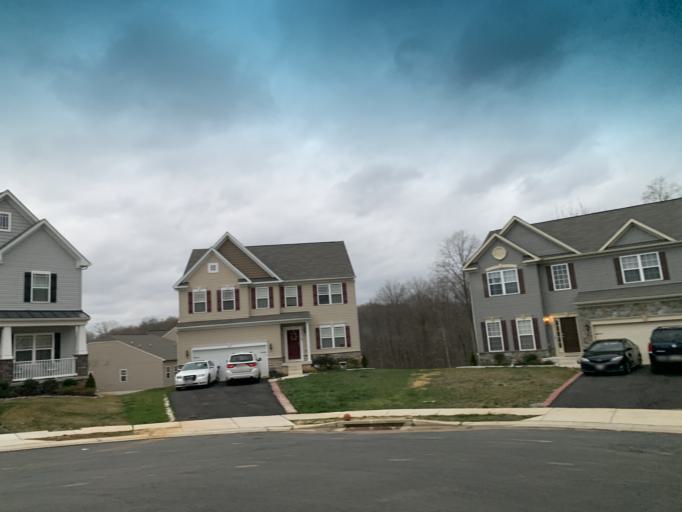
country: US
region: Maryland
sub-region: Harford County
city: Perryman
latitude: 39.5025
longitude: -76.2098
